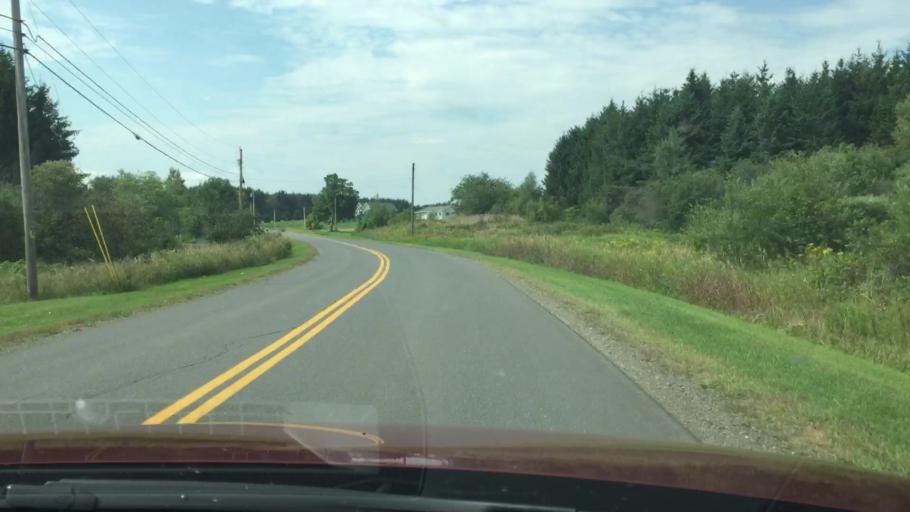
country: US
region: Maine
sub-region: Aroostook County
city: Caribou
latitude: 46.8287
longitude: -68.0191
